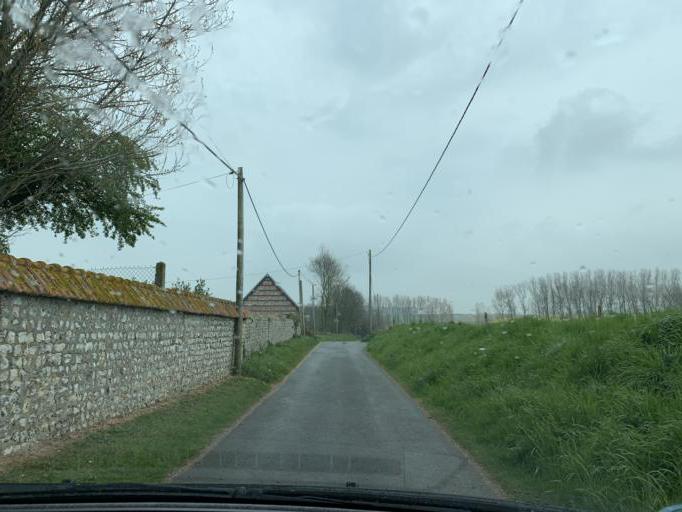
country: FR
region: Haute-Normandie
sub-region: Departement de la Seine-Maritime
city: Etretat
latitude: 49.6850
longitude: 0.1807
